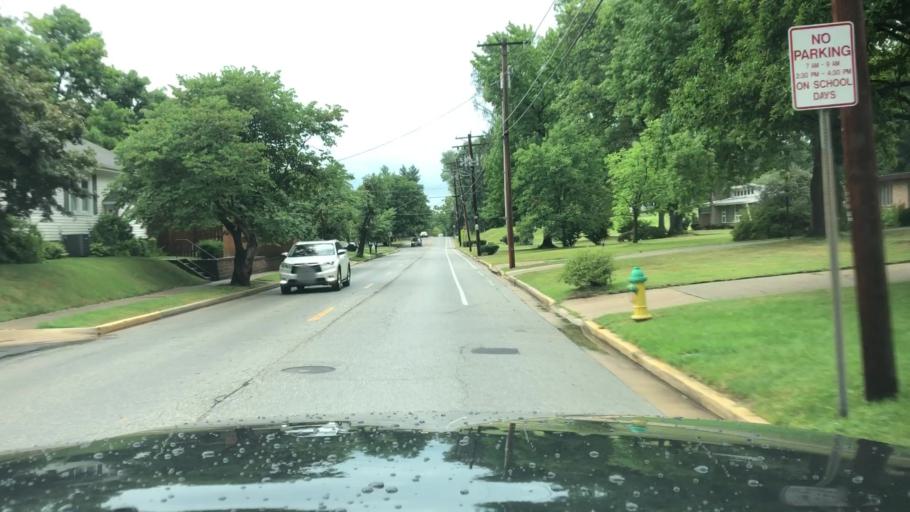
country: US
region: Missouri
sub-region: Saint Charles County
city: Saint Charles
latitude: 38.7891
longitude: -90.4963
